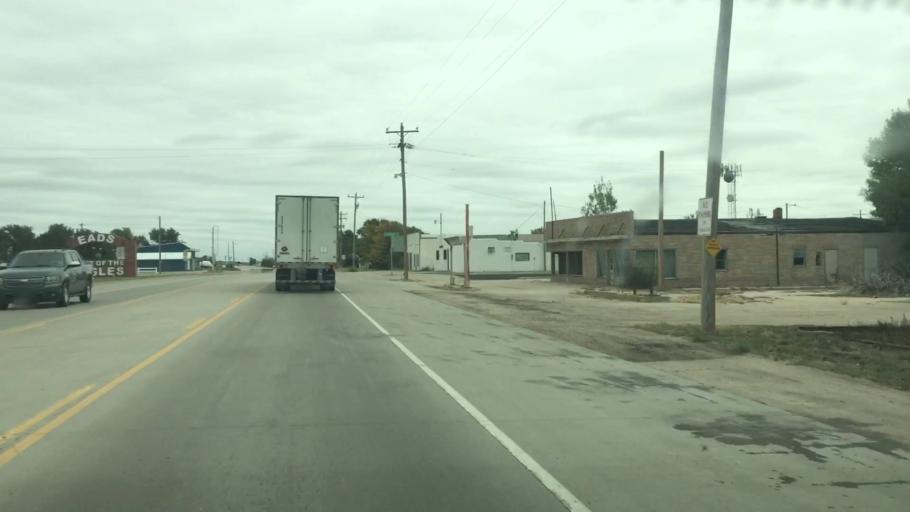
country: US
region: Colorado
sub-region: Kiowa County
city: Eads
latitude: 38.4777
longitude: -102.7799
